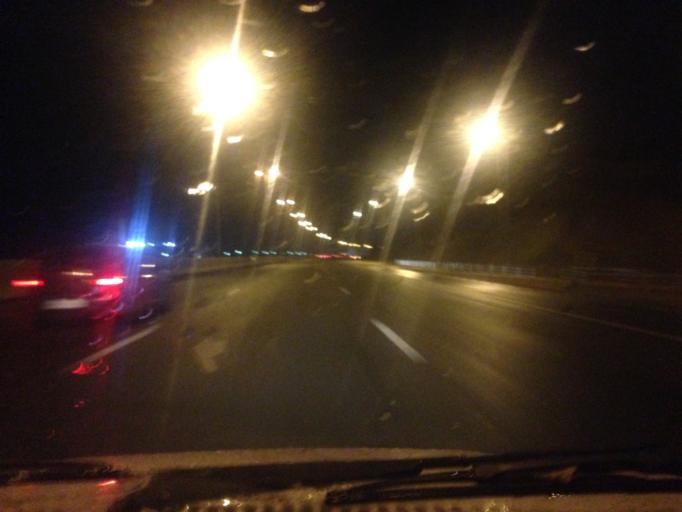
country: IR
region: Tehran
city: Eslamshahr
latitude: 35.4395
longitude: 51.2046
